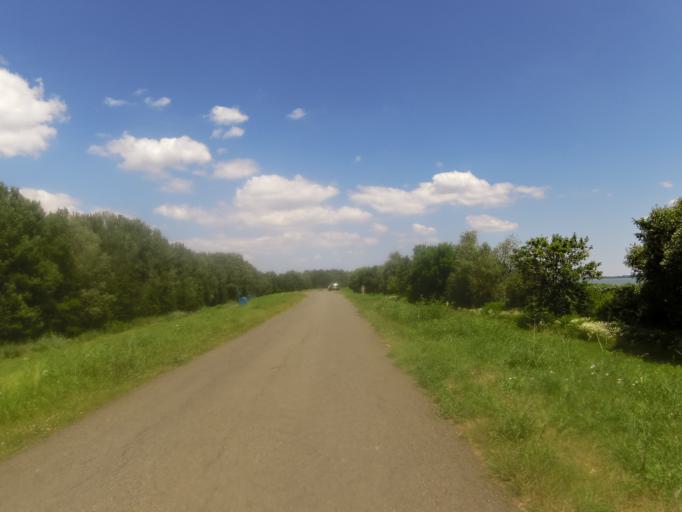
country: HU
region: Heves
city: Tiszanana
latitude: 47.5581
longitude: 20.6068
